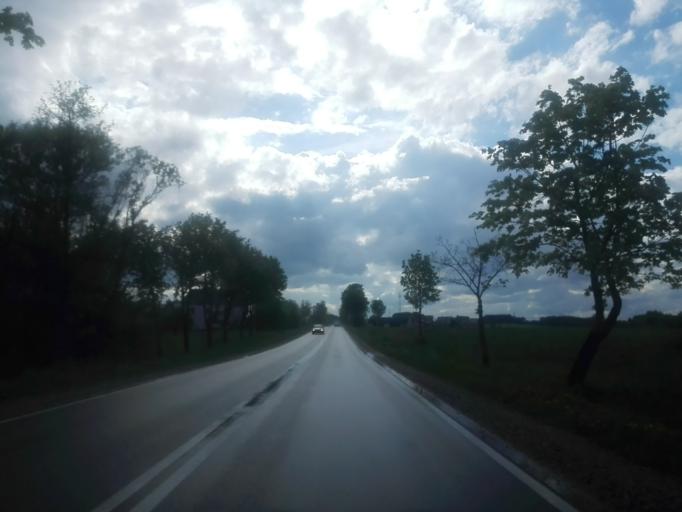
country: PL
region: Podlasie
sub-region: Powiat lomzynski
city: Wizna
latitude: 53.2018
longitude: 22.3953
